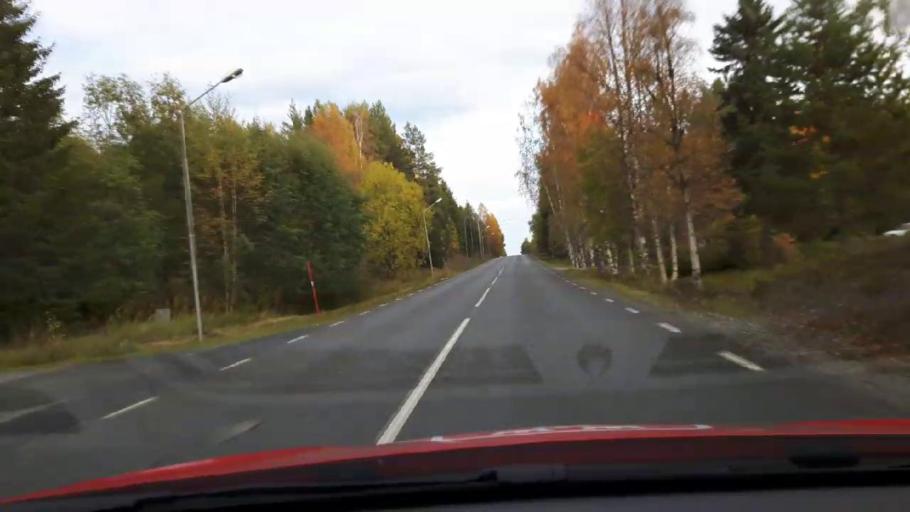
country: SE
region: Jaemtland
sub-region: Krokoms Kommun
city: Krokom
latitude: 63.3524
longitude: 14.5451
